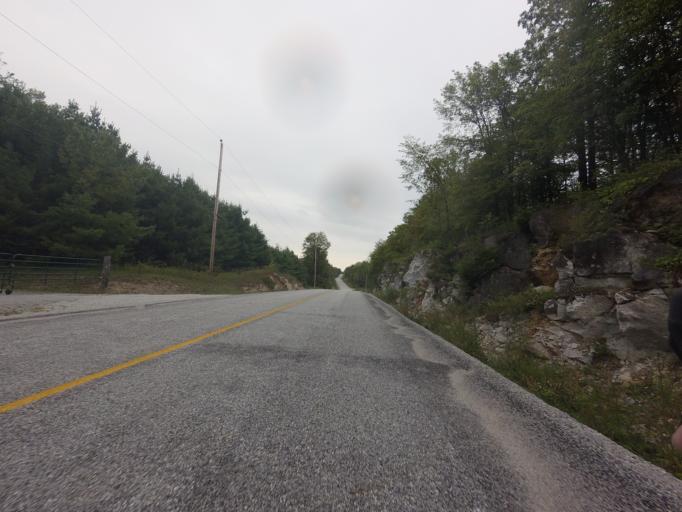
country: CA
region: Ontario
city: Perth
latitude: 44.8927
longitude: -76.5070
